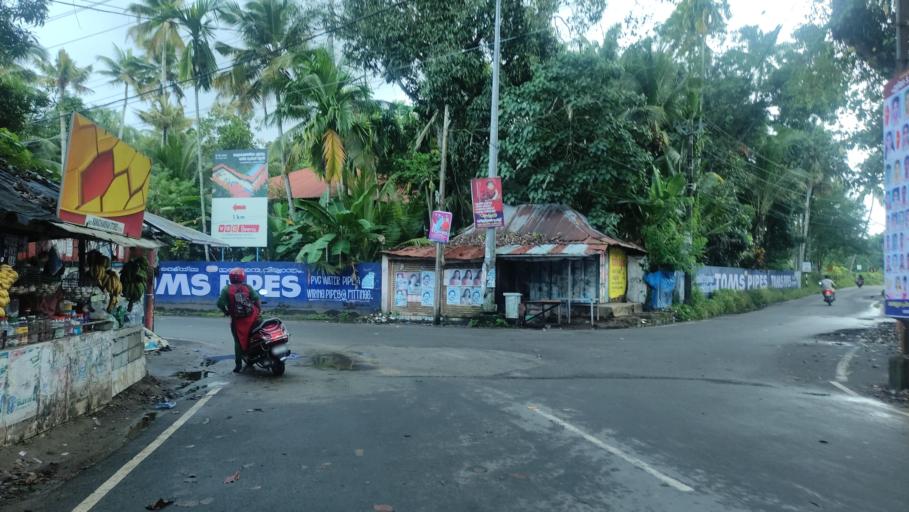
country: IN
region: Kerala
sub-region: Alappuzha
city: Kayankulam
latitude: 9.1934
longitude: 76.4995
